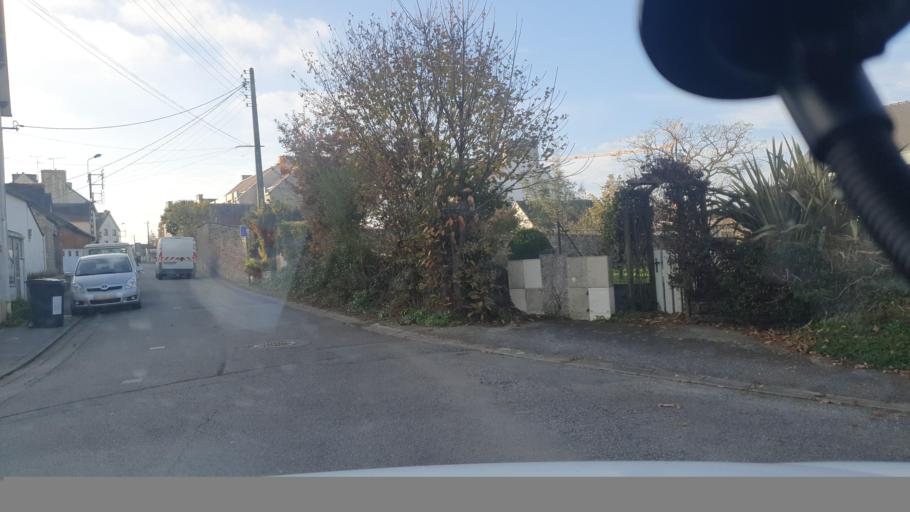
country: FR
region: Brittany
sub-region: Departement du Finistere
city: Briec
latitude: 48.1021
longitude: -3.9933
